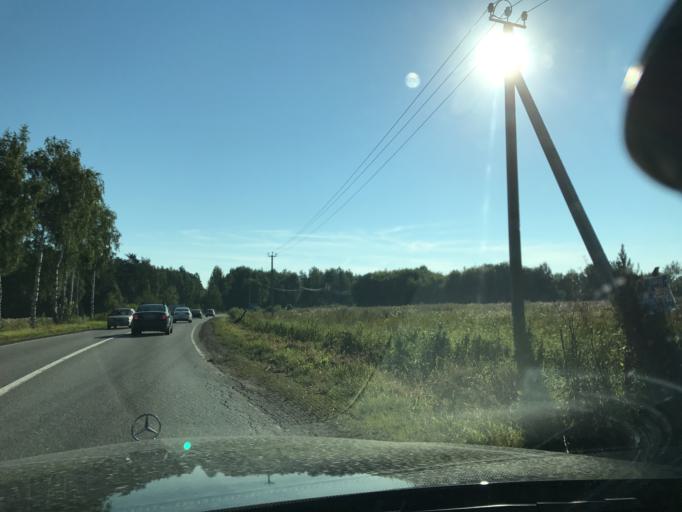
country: RU
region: Moskovskaya
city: Bakhchivandzhi
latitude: 55.8484
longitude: 38.1029
